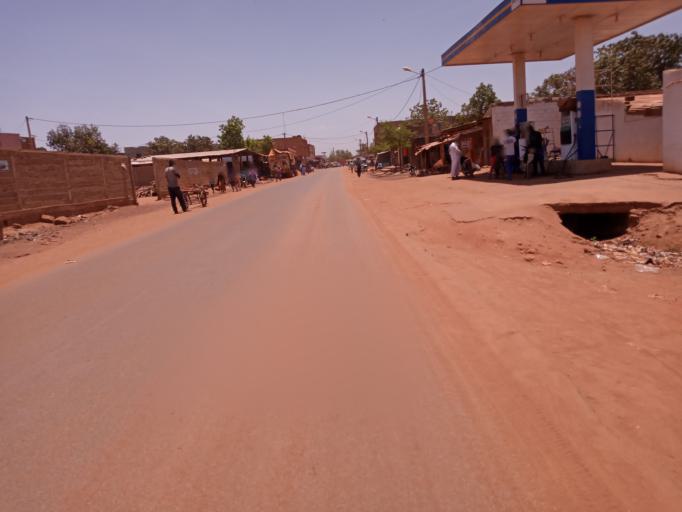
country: ML
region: Bamako
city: Bamako
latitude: 12.5759
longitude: -7.9705
